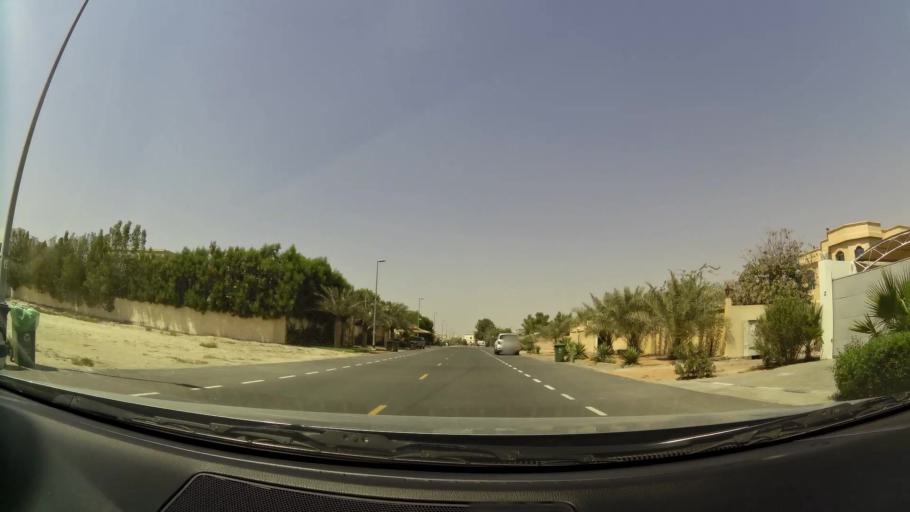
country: AE
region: Dubai
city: Dubai
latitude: 25.1070
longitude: 55.2159
